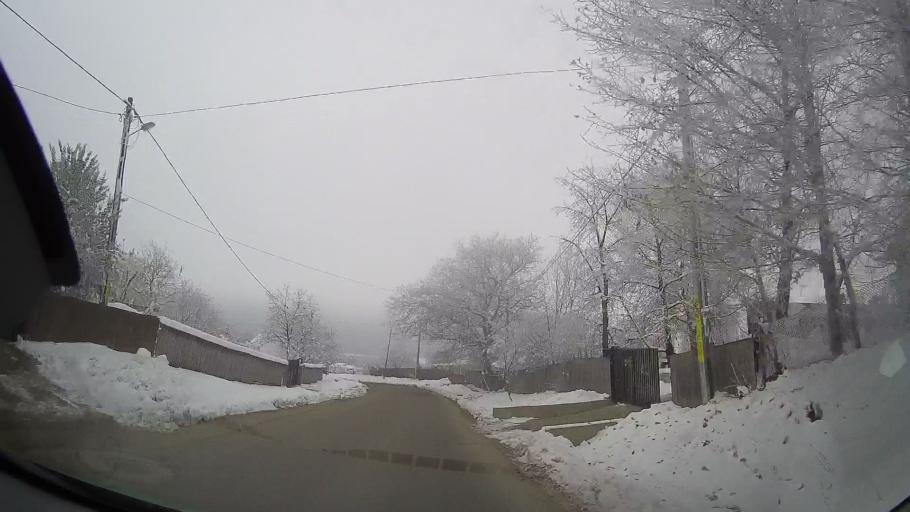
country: RO
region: Neamt
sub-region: Comuna Poenari
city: Poienari
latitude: 46.8880
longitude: 27.1326
